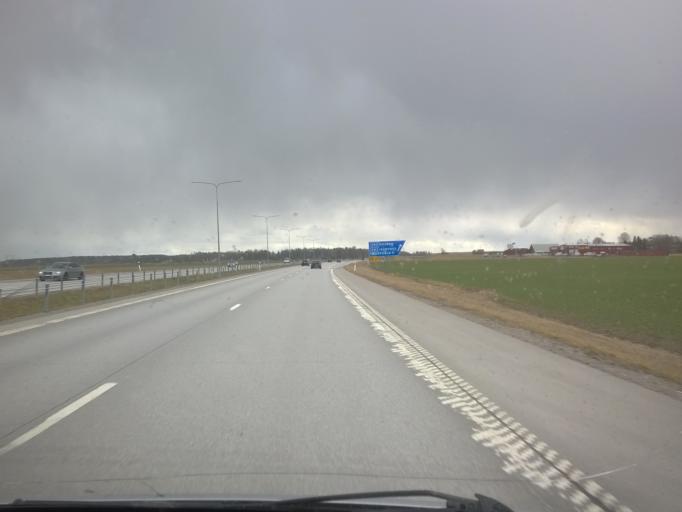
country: SE
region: Uppsala
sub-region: Uppsala Kommun
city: Saevja
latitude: 59.8525
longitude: 17.7330
